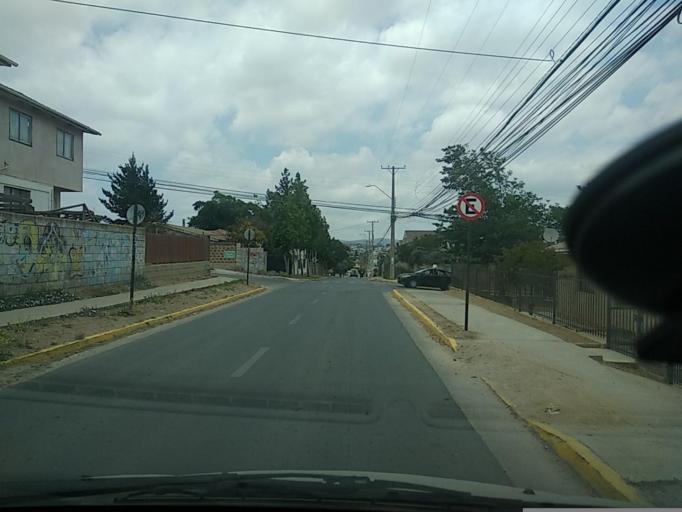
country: CL
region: Valparaiso
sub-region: Provincia de Marga Marga
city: Villa Alemana
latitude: -33.0357
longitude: -71.4044
